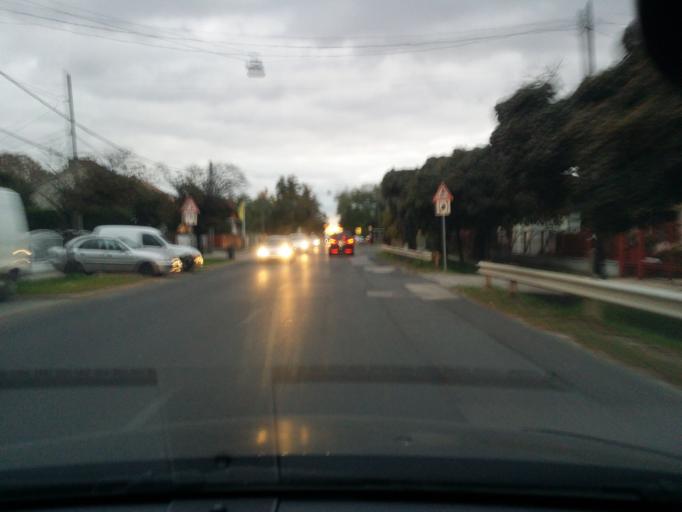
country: HU
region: Budapest
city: Budapest XVI. keruelet
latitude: 47.5225
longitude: 19.1541
